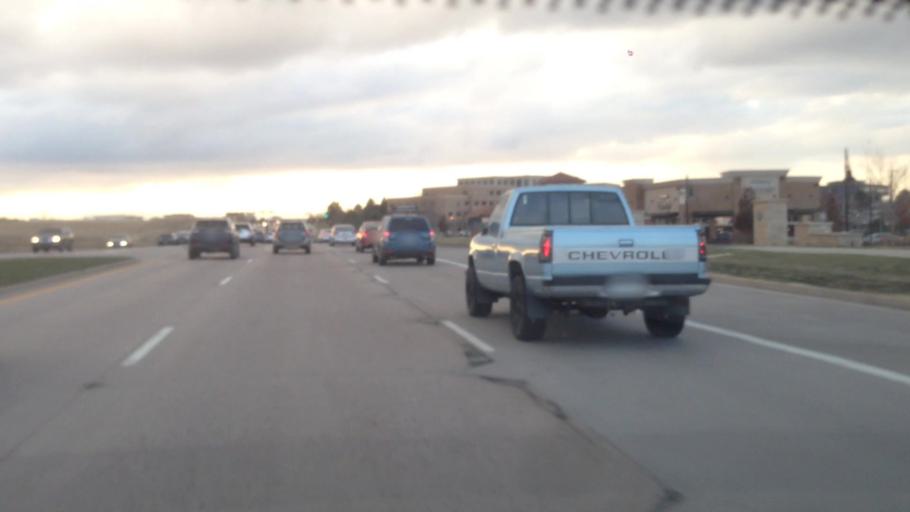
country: US
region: Colorado
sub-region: Douglas County
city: Meridian
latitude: 39.5363
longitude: -104.8561
